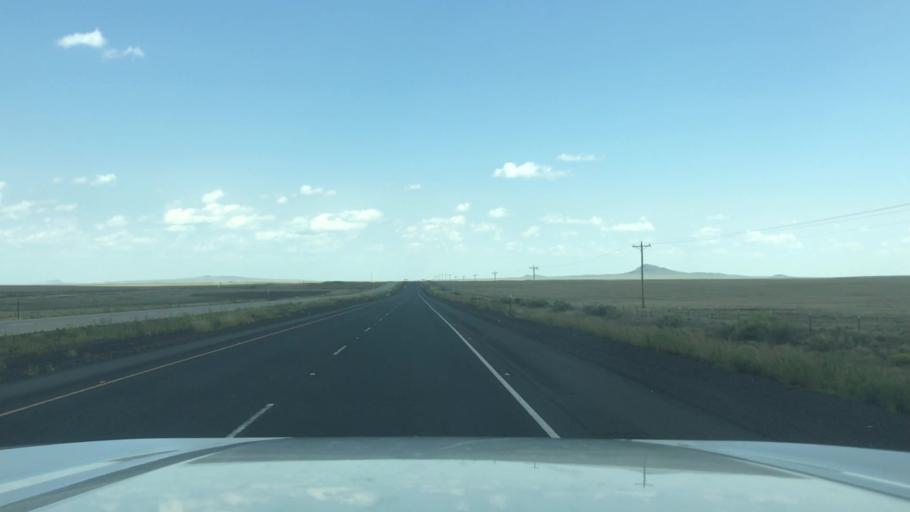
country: US
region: New Mexico
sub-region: Union County
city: Clayton
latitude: 36.6285
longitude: -103.7089
